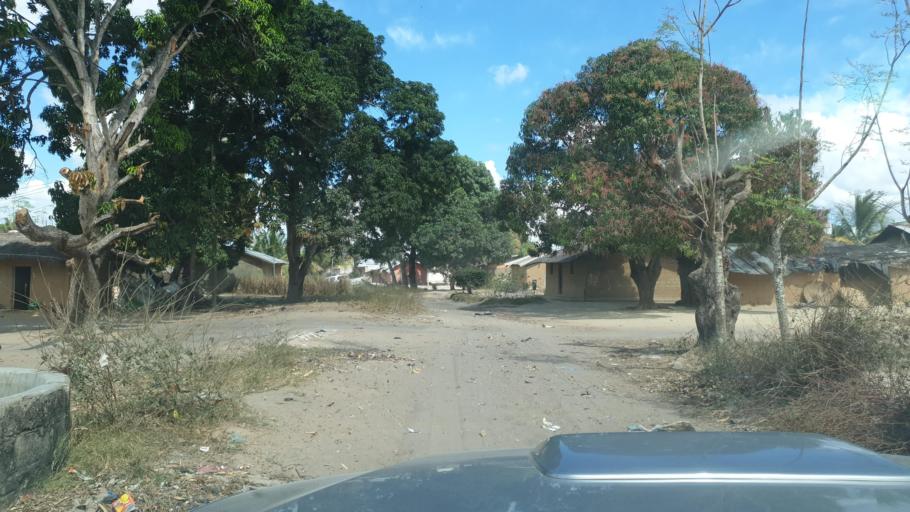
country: MZ
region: Nampula
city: Nacala
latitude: -14.5726
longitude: 40.6966
